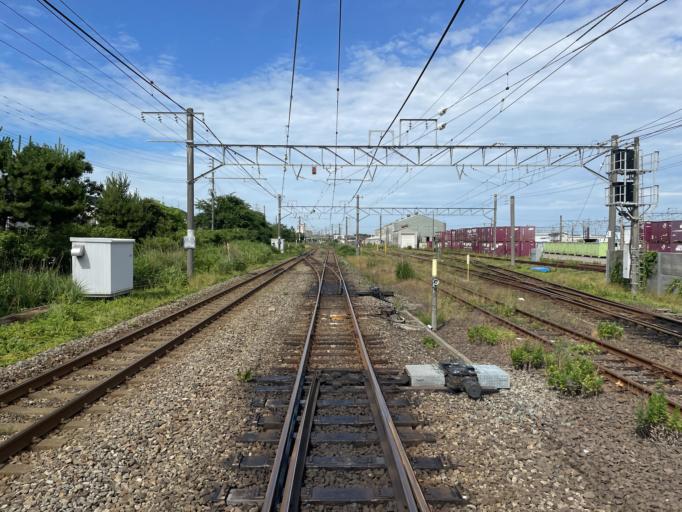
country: JP
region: Niigata
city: Kameda-honcho
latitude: 37.9071
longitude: 139.1040
